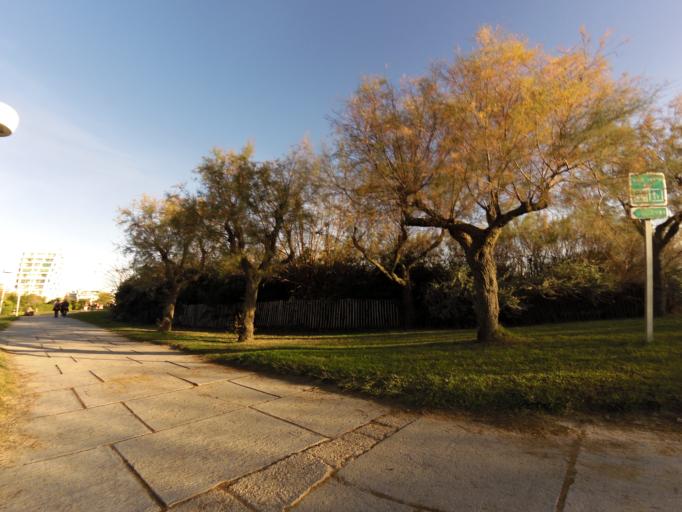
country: FR
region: Languedoc-Roussillon
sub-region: Departement de l'Herault
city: La Grande-Motte
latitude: 43.5582
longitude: 4.0609
